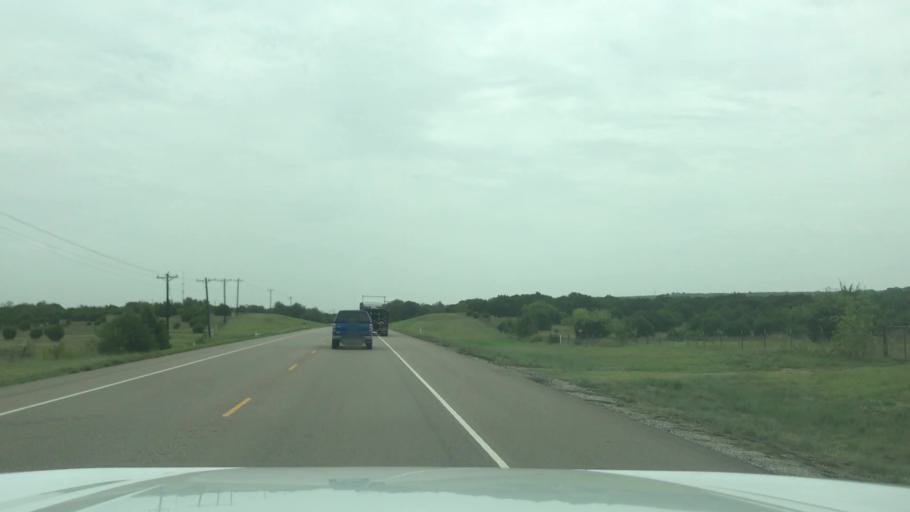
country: US
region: Texas
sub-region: Bosque County
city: Meridian
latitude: 31.9268
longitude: -97.6860
